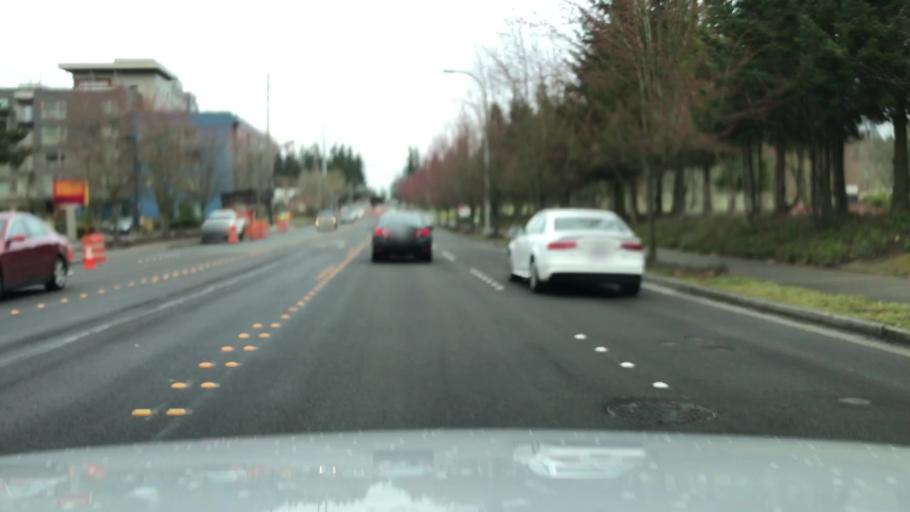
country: US
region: Washington
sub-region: King County
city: Redmond
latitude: 47.6289
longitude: -122.1323
